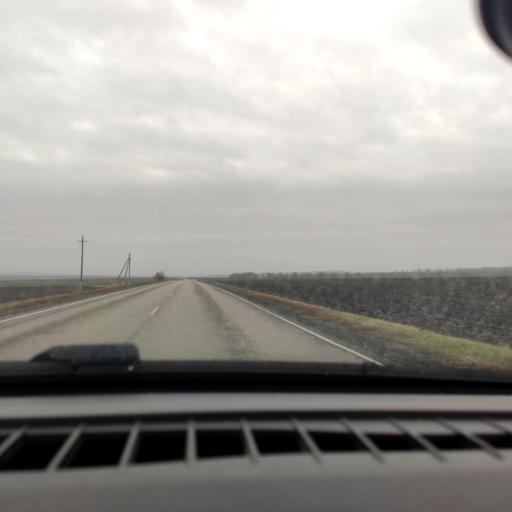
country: RU
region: Belgorod
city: Ilovka
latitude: 50.7790
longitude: 38.8060
